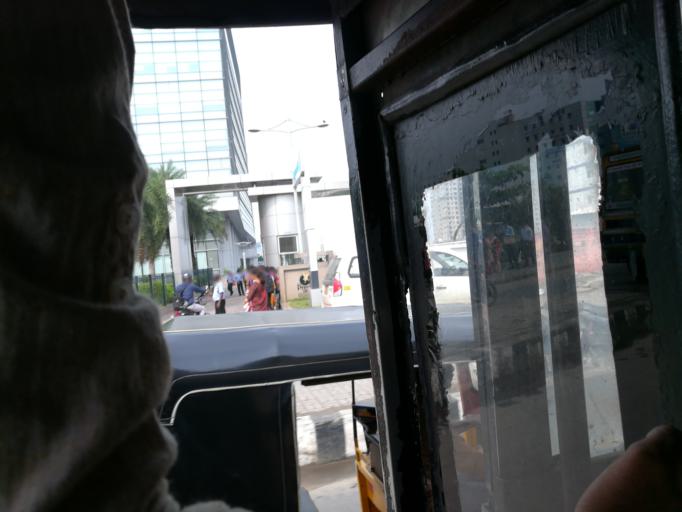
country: IN
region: Tamil Nadu
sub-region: Kancheepuram
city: Injambakkam
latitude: 12.9121
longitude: 80.2290
